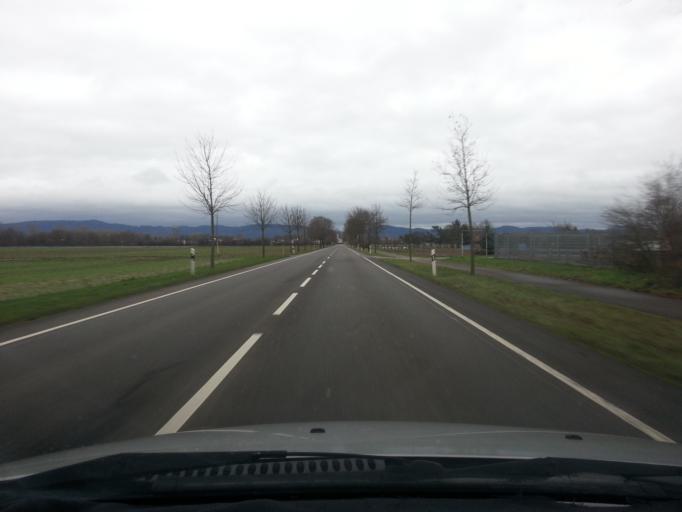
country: DE
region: Hesse
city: Lorsch
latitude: 49.5992
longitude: 8.5696
